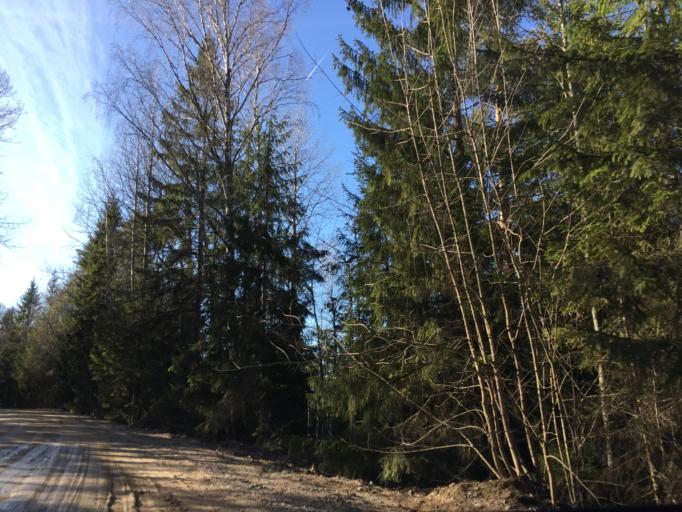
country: LV
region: Ropazu
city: Ropazi
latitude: 56.9197
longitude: 24.7372
